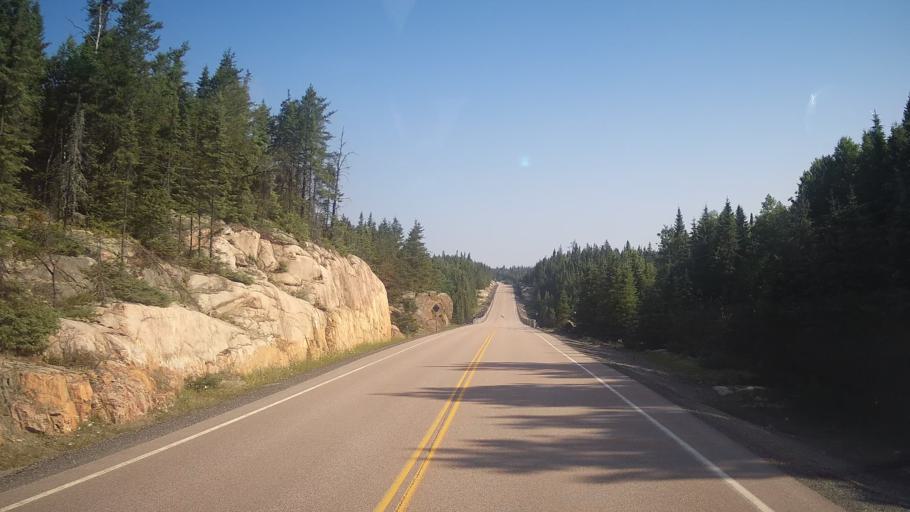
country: CA
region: Ontario
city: Rayside-Balfour
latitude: 47.0289
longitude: -81.6369
